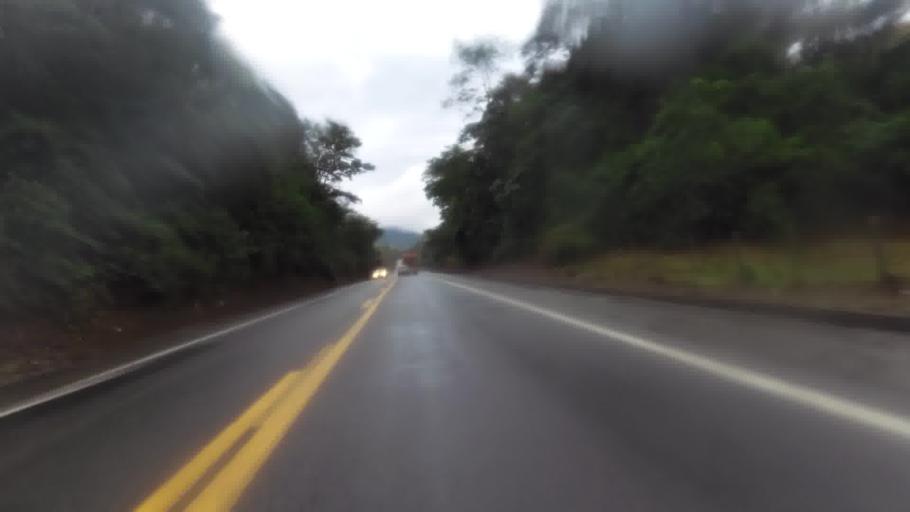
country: BR
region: Espirito Santo
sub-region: Mimoso Do Sul
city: Mimoso do Sul
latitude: -21.0301
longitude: -41.1794
